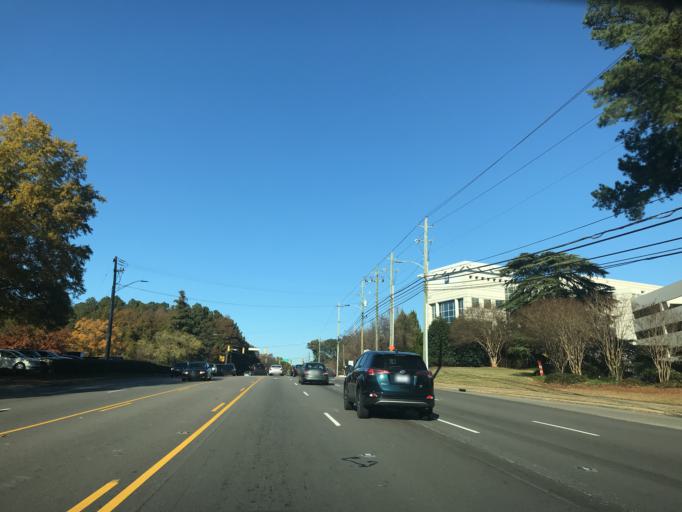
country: US
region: North Carolina
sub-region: Wake County
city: Raleigh
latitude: 35.8293
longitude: -78.6194
